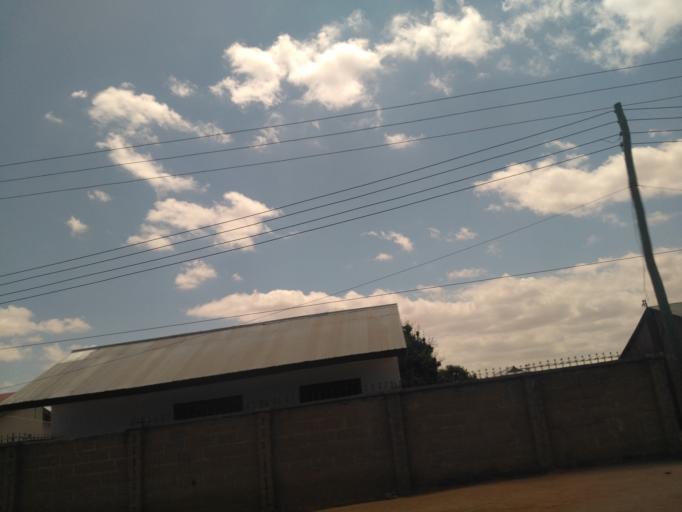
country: TZ
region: Dodoma
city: Kisasa
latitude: -6.1668
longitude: 35.7732
